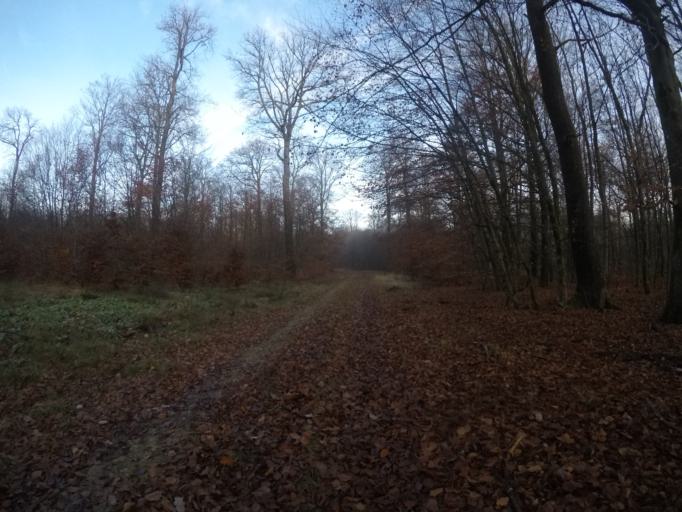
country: BE
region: Wallonia
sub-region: Province du Luxembourg
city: Habay-la-Vieille
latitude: 49.7509
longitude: 5.6716
